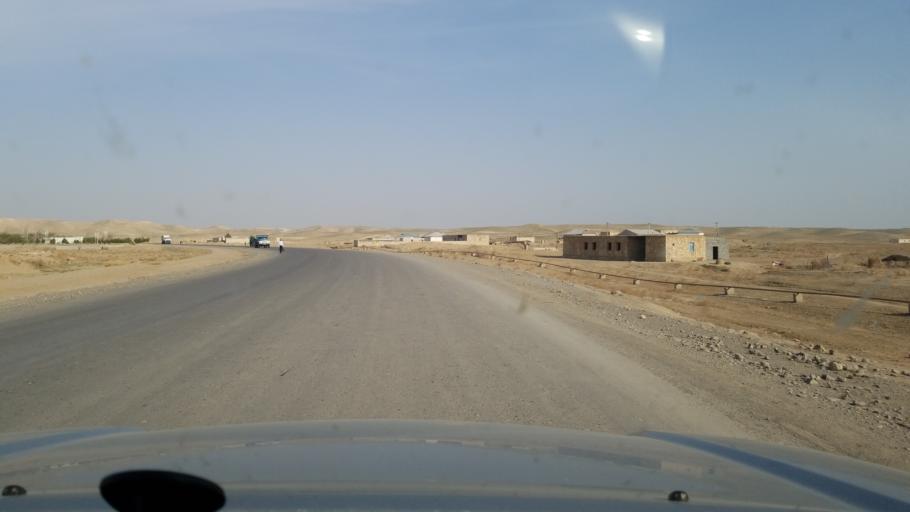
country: AF
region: Jowzjan
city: Khamyab
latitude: 37.6607
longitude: 65.6153
